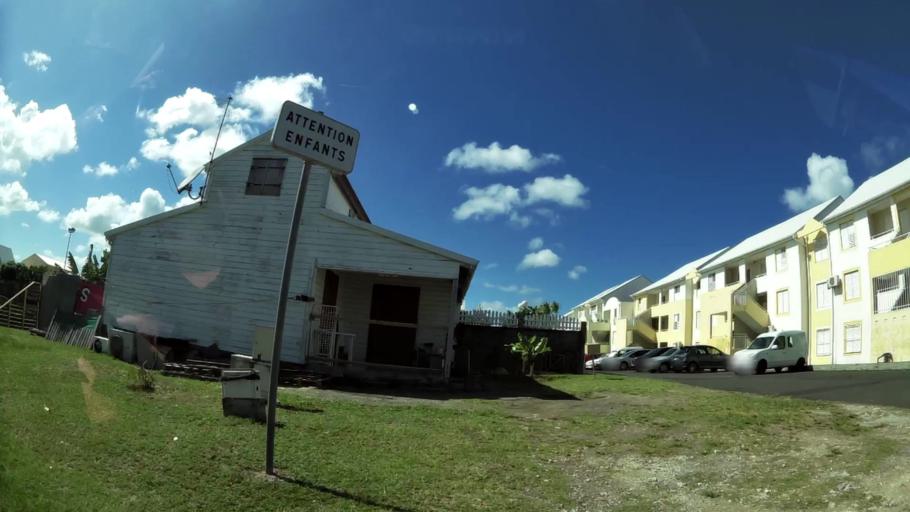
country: GP
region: Guadeloupe
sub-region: Guadeloupe
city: Le Moule
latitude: 16.3279
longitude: -61.3510
